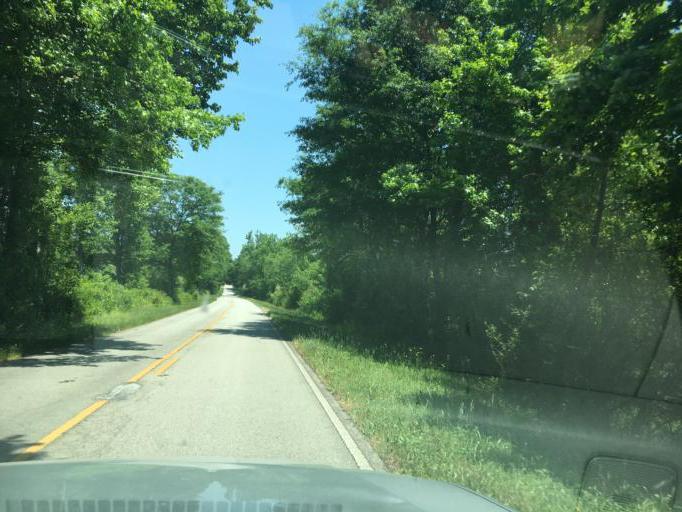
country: US
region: Georgia
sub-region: Hart County
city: Royston
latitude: 34.3104
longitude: -83.0914
